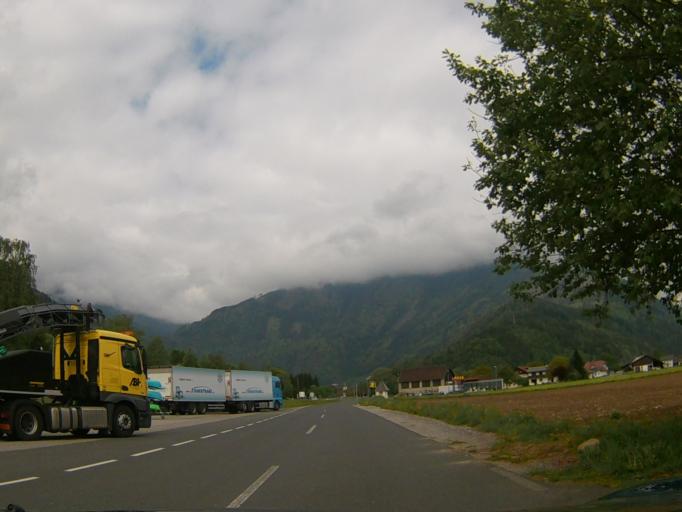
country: AT
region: Carinthia
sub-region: Politischer Bezirk Spittal an der Drau
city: Sachsenburg
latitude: 46.8325
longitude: 13.3844
